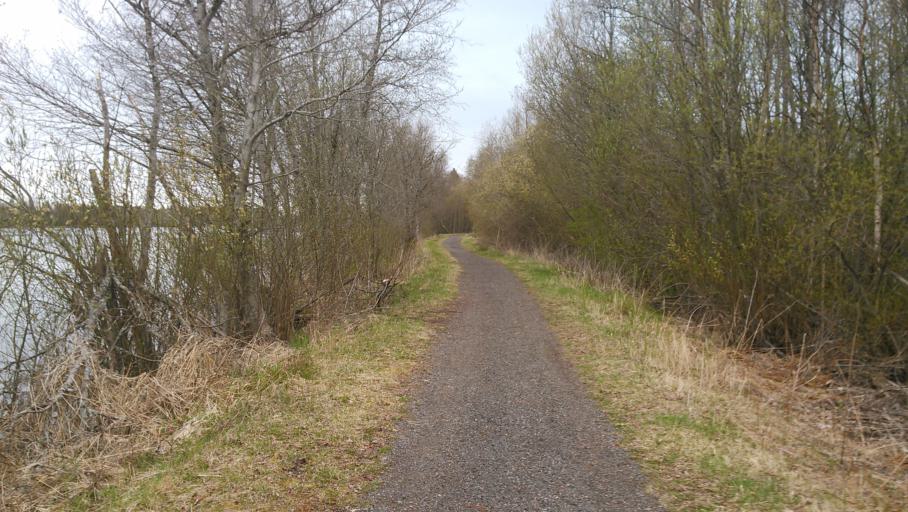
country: SE
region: Vaesterbotten
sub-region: Umea Kommun
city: Umea
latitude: 63.7840
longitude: 20.3136
